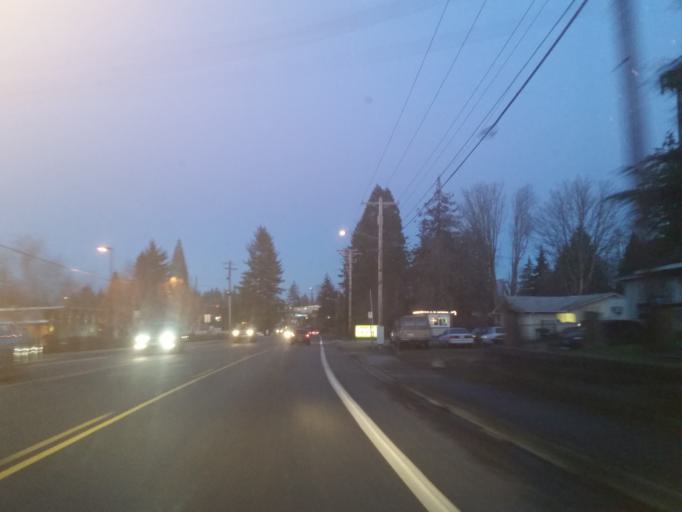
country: US
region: Washington
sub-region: Snohomish County
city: Martha Lake
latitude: 47.8801
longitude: -122.2848
